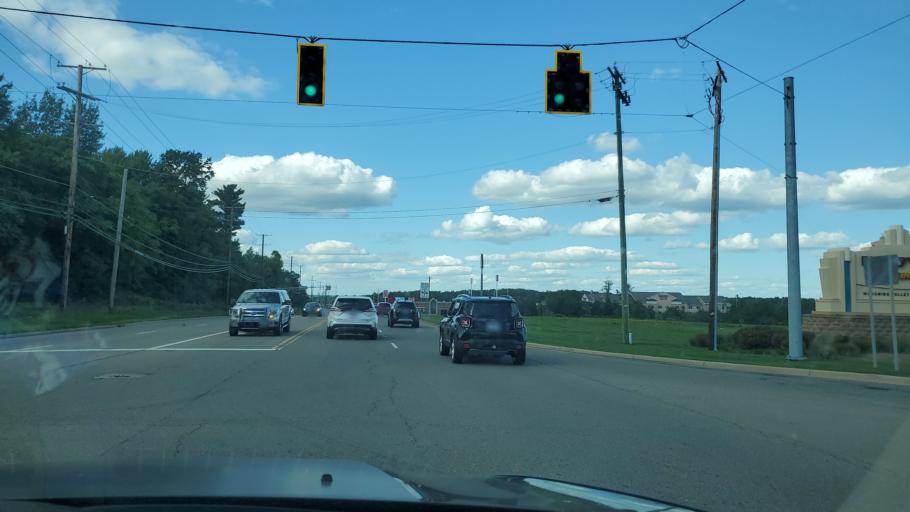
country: US
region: Ohio
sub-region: Mahoning County
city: Austintown
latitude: 41.1167
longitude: -80.7680
